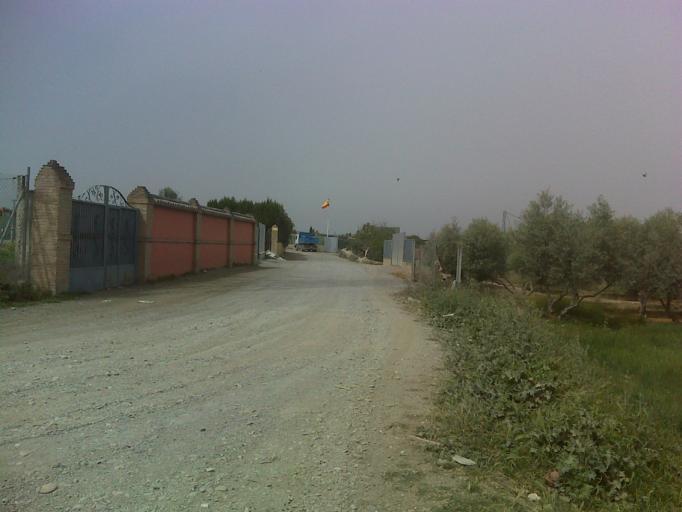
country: ES
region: Andalusia
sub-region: Provincia de Granada
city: Churriana de la Vega
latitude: 37.1564
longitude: -3.6542
